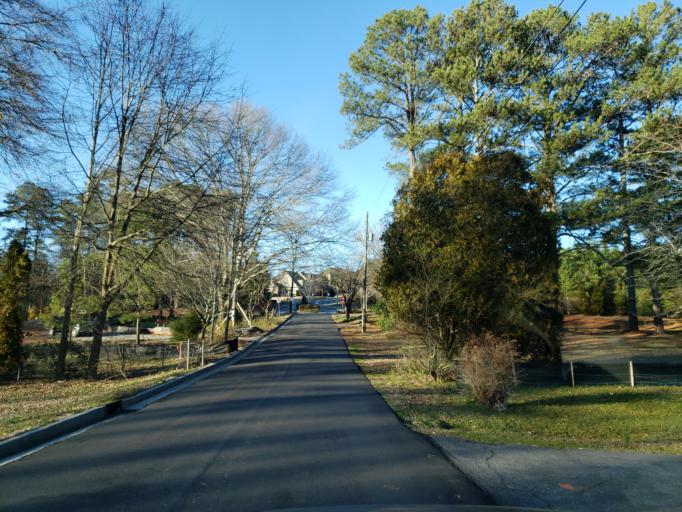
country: US
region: Georgia
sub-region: Cherokee County
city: Woodstock
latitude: 34.1076
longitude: -84.5159
